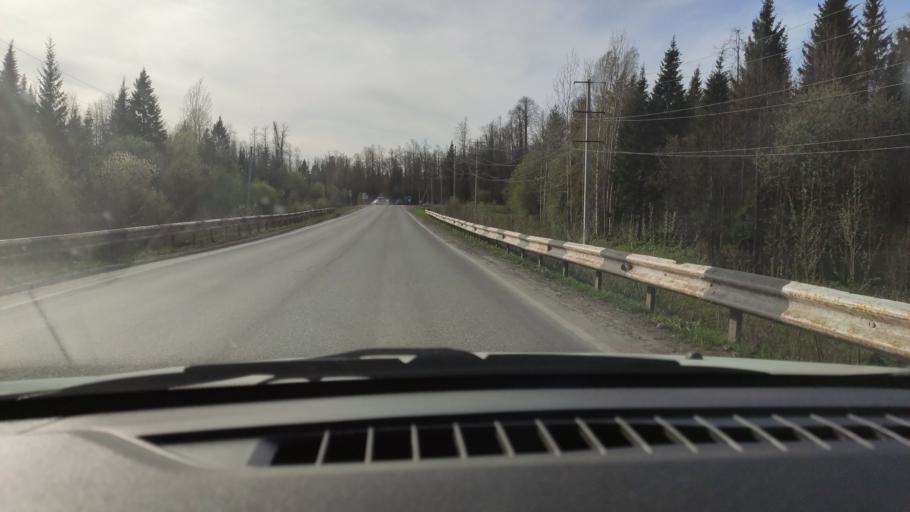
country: RU
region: Perm
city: Novyye Lyady
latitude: 57.9542
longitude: 56.5188
